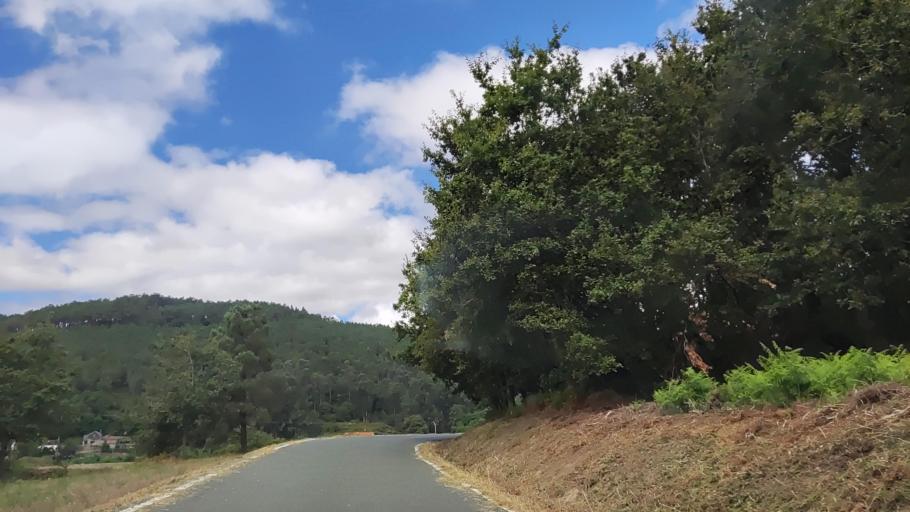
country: ES
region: Galicia
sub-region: Provincia da Coruna
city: Rois
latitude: 42.7478
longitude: -8.7004
